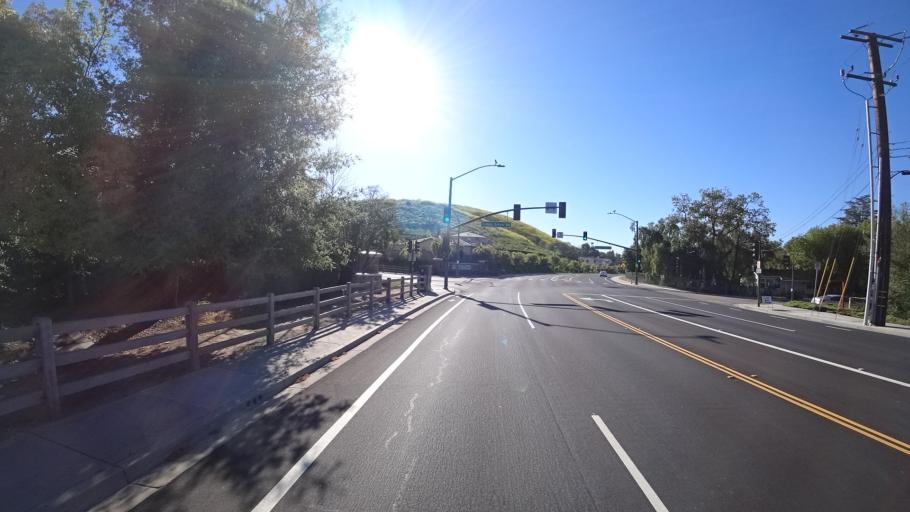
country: US
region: California
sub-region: Ventura County
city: Thousand Oaks
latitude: 34.1796
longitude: -118.8415
